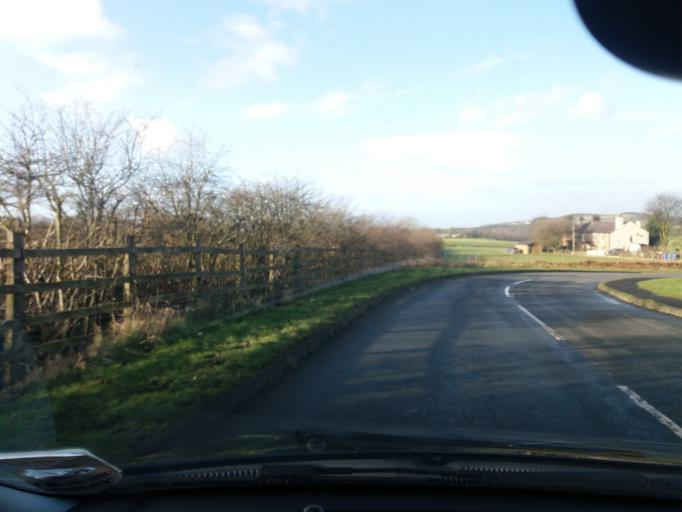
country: GB
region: England
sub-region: Lancashire
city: Adlington
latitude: 53.6276
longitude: -2.5860
